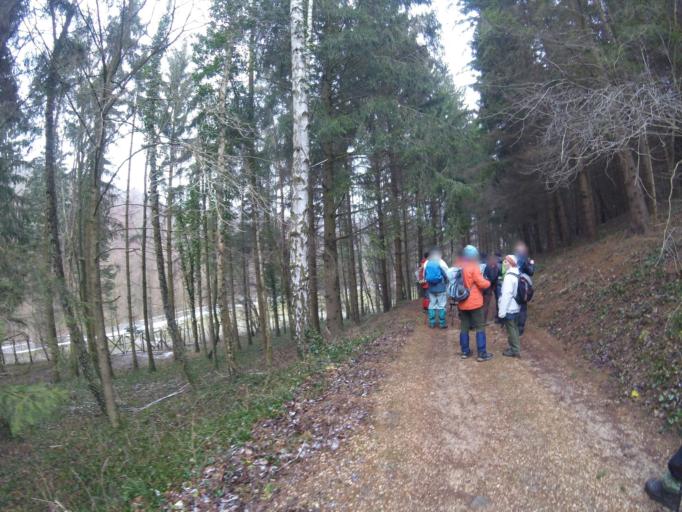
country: HU
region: Pest
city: Visegrad
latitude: 47.7680
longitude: 18.9828
